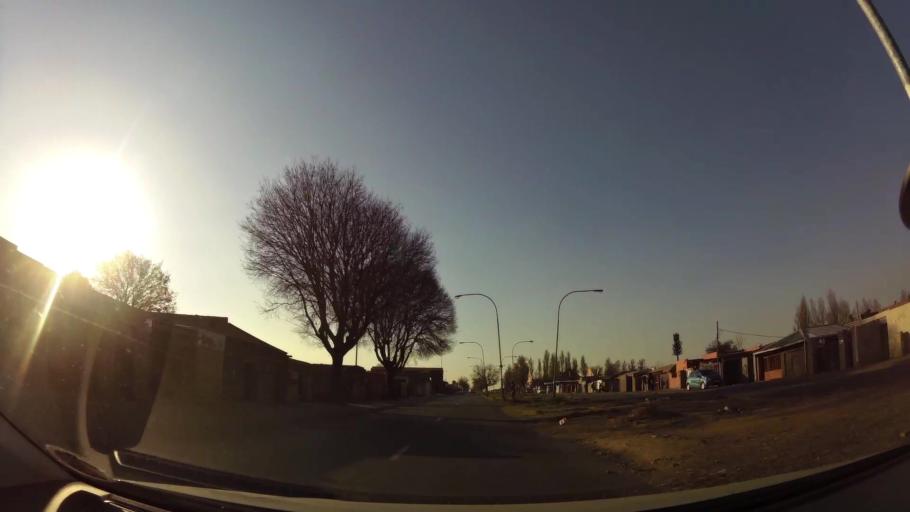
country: ZA
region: Gauteng
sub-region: City of Johannesburg Metropolitan Municipality
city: Soweto
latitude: -26.2542
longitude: 27.8777
